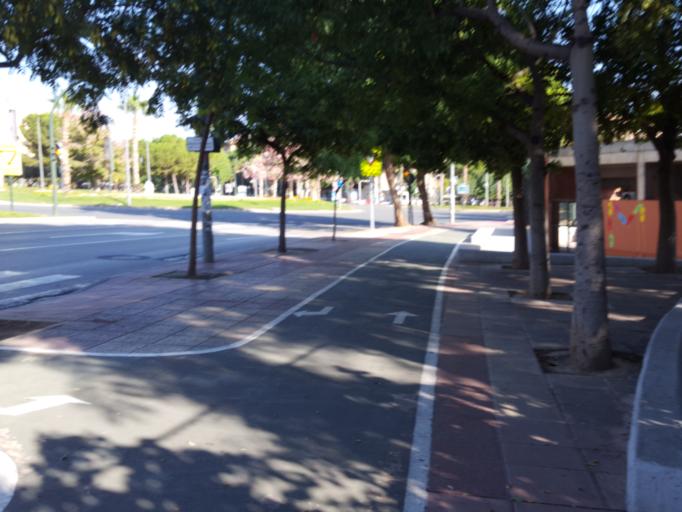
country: ES
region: Murcia
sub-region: Murcia
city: Murcia
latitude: 37.9964
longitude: -1.1356
